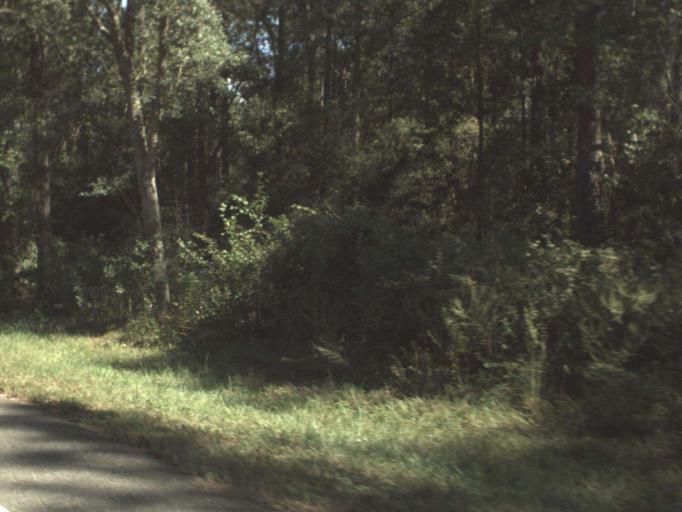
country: US
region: Alabama
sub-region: Geneva County
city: Samson
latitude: 30.9862
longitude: -86.1336
